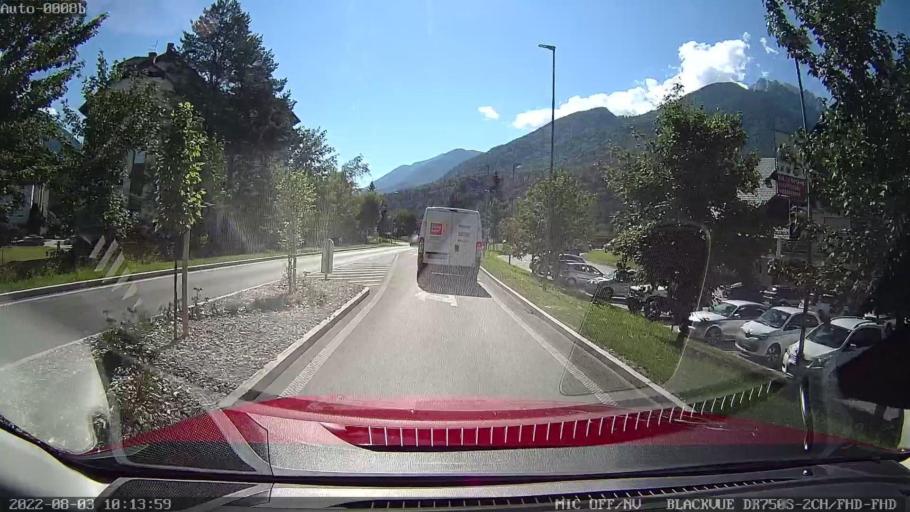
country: SI
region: Kranjska Gora
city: Kranjska Gora
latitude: 46.4888
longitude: 13.7965
